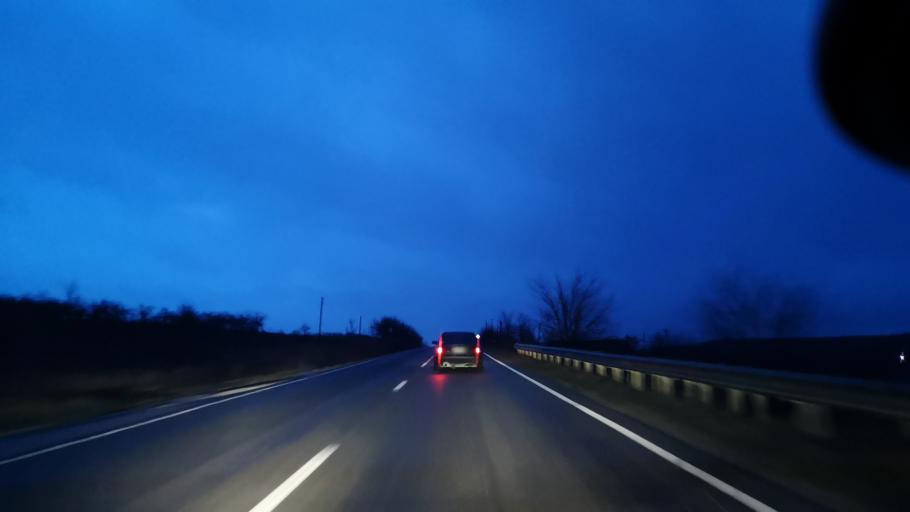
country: MD
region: Orhei
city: Orhei
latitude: 47.4127
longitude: 28.8126
